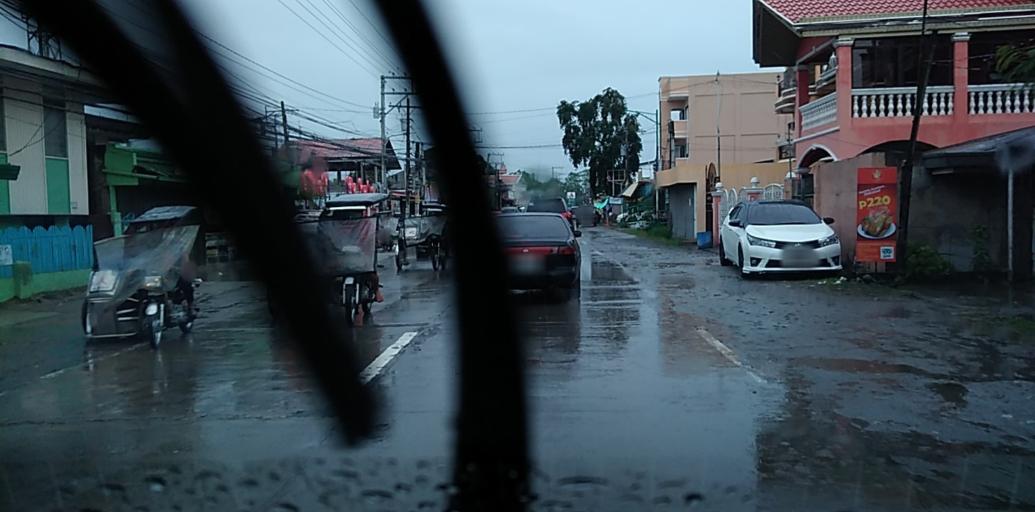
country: PH
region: Central Luzon
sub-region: Province of Pampanga
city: Mexico
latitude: 15.0594
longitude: 120.7188
